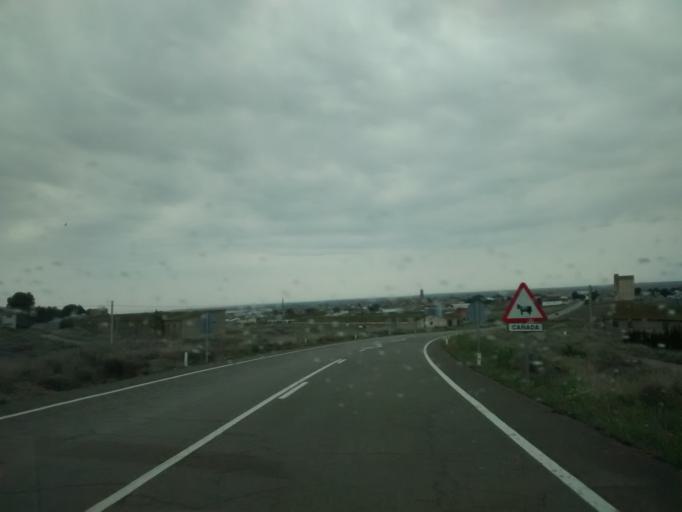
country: ES
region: Aragon
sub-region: Provincia de Zaragoza
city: Bujaraloz
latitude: 41.5058
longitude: -0.1616
